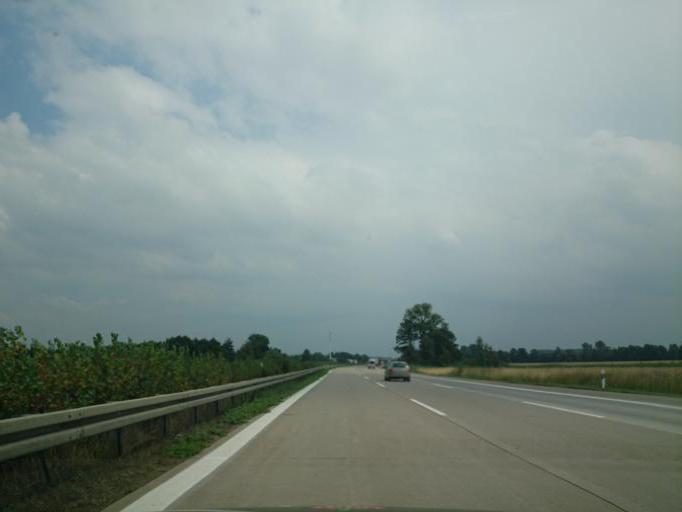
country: DE
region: Brandenburg
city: Ludwigsfelde
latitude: 52.3009
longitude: 13.1525
